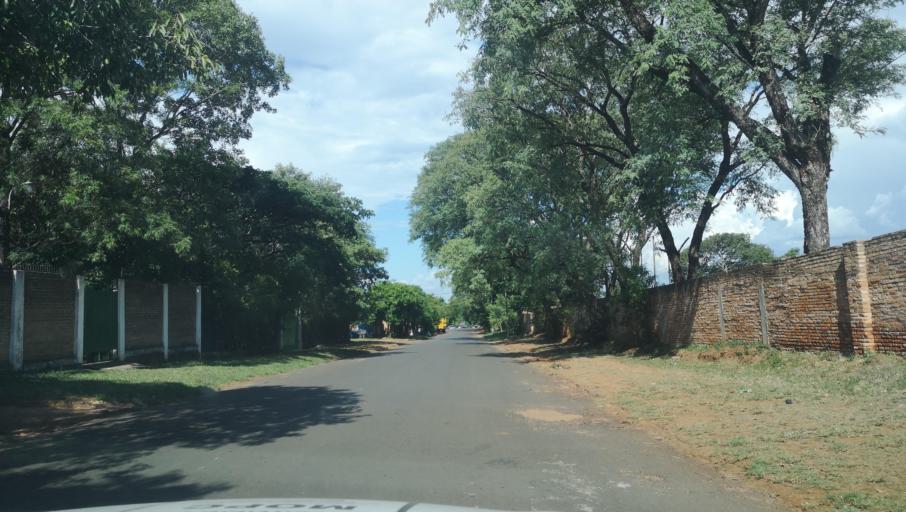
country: PY
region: Misiones
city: Santa Maria
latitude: -26.8845
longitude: -57.0339
